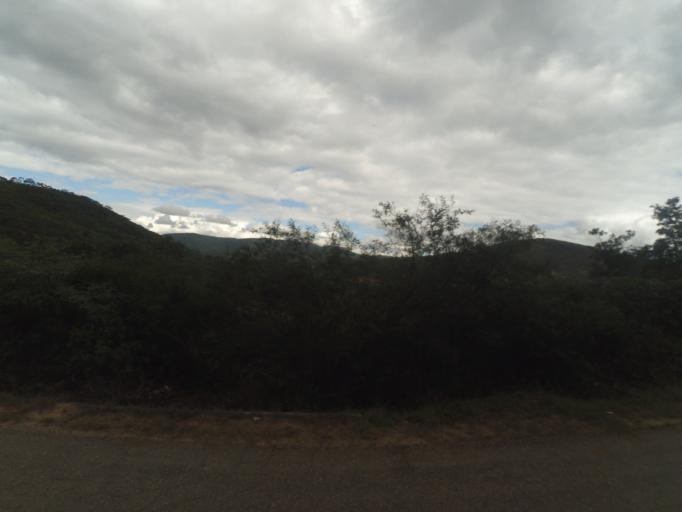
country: BO
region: Santa Cruz
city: Samaipata
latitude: -18.1708
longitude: -63.8383
